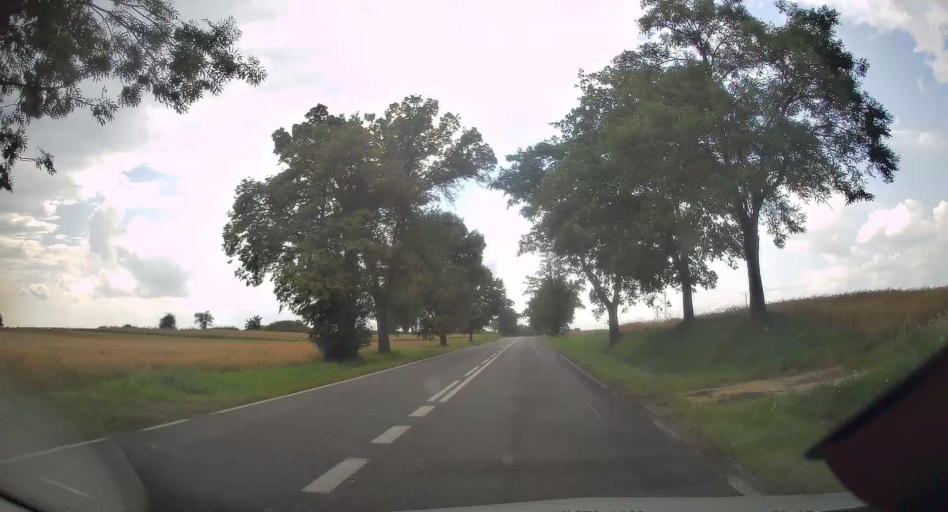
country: PL
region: Lodz Voivodeship
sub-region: Powiat skierniewicki
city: Gluchow
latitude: 51.7784
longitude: 20.0956
